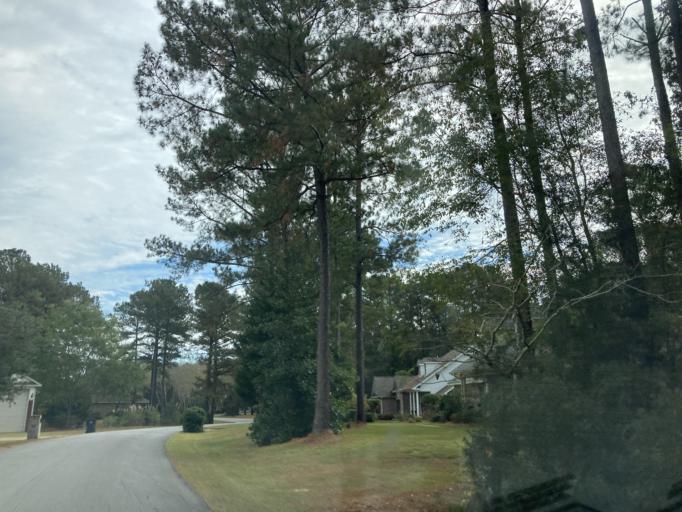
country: US
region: Mississippi
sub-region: Lamar County
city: West Hattiesburg
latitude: 31.3307
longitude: -89.4135
